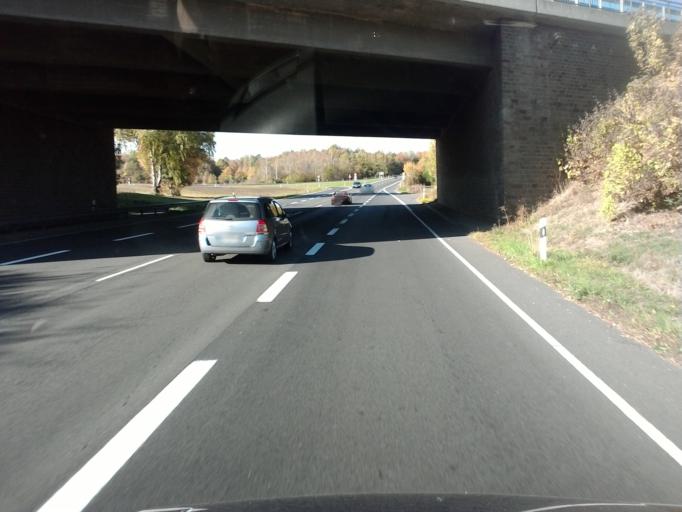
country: DE
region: Rheinland-Pfalz
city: Bitburg
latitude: 49.9592
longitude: 6.5162
